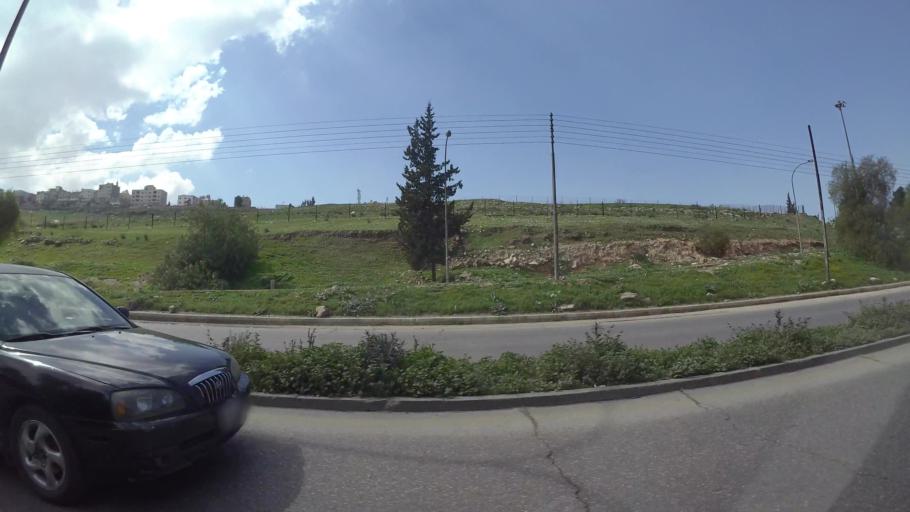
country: JO
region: Amman
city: Amman
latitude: 31.9877
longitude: 35.9771
